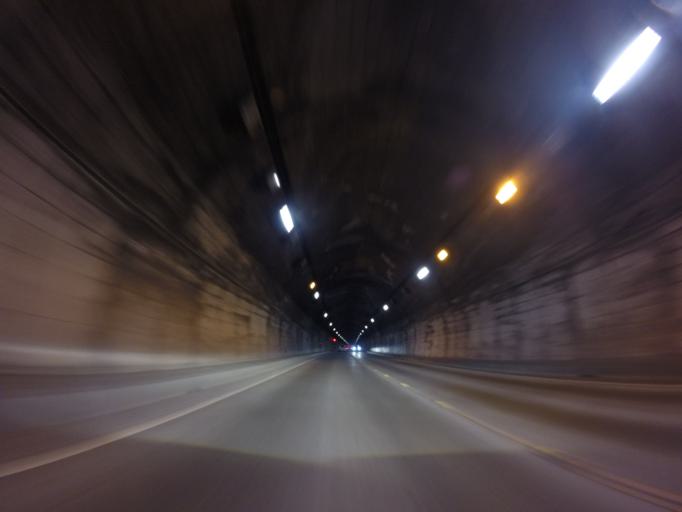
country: JP
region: Shizuoka
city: Mishima
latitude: 35.0611
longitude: 138.9230
